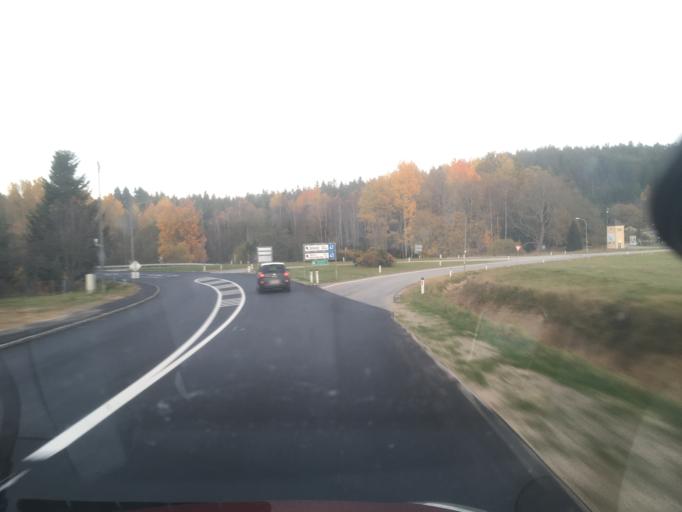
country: AT
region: Lower Austria
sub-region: Politischer Bezirk Zwettl
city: Langschlag
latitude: 48.5928
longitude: 14.7564
